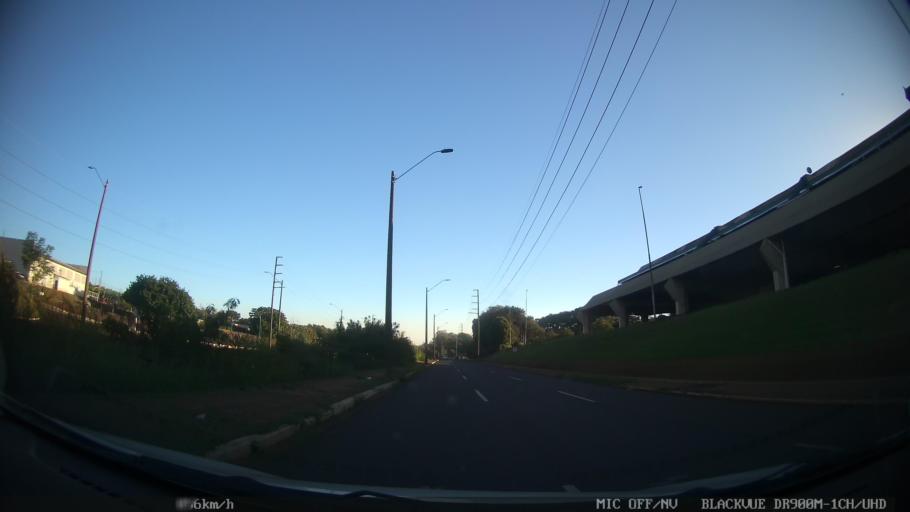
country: BR
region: Sao Paulo
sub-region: Araraquara
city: Araraquara
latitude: -21.8079
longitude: -48.1742
